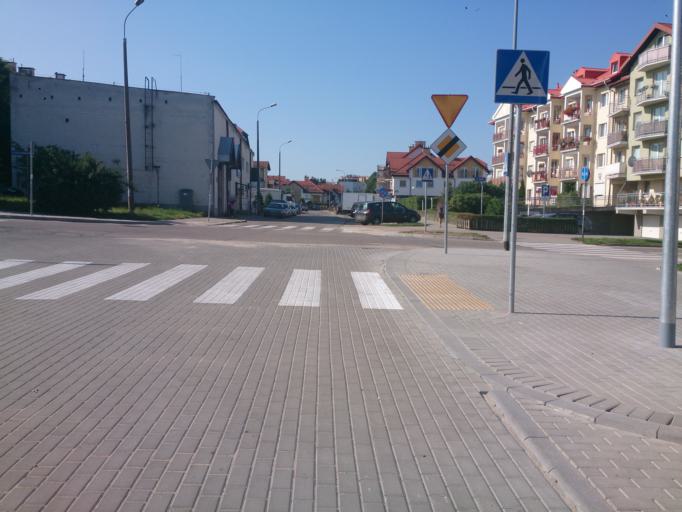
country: PL
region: Pomeranian Voivodeship
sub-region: Gdynia
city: Wielki Kack
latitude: 54.4688
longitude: 18.4863
